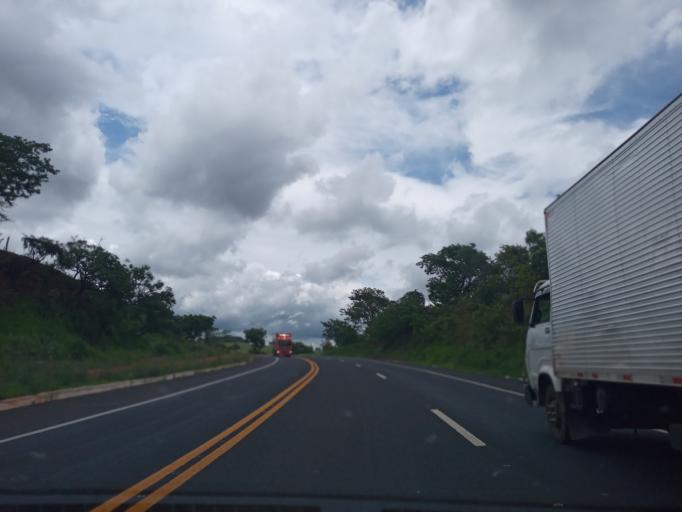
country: BR
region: Minas Gerais
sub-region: Monte Carmelo
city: Monte Carmelo
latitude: -19.2607
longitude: -47.6505
